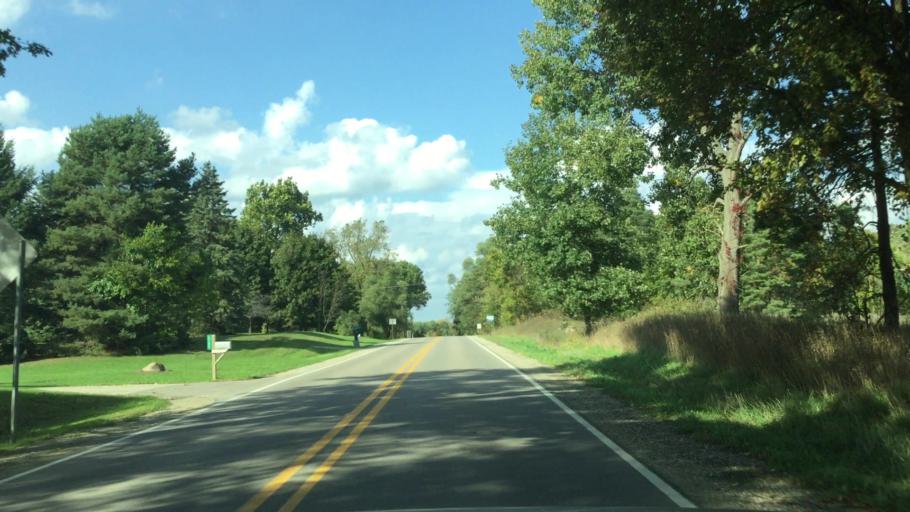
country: US
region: Michigan
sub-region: Oakland County
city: Milford
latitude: 42.6366
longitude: -83.6993
